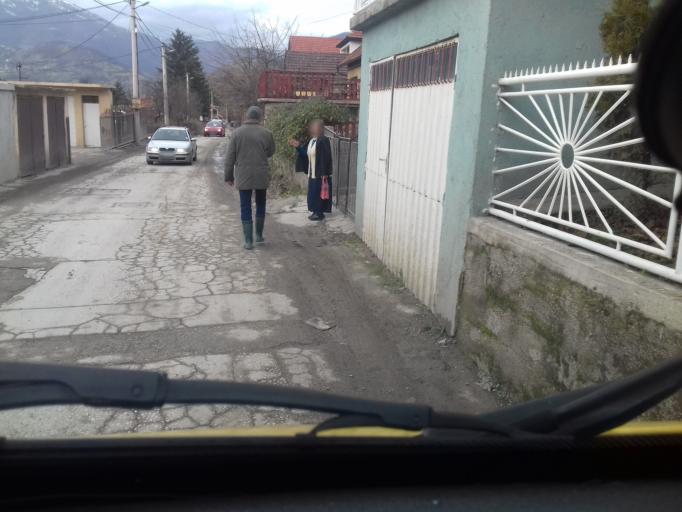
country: BA
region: Federation of Bosnia and Herzegovina
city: Zenica
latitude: 44.2226
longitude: 17.9142
